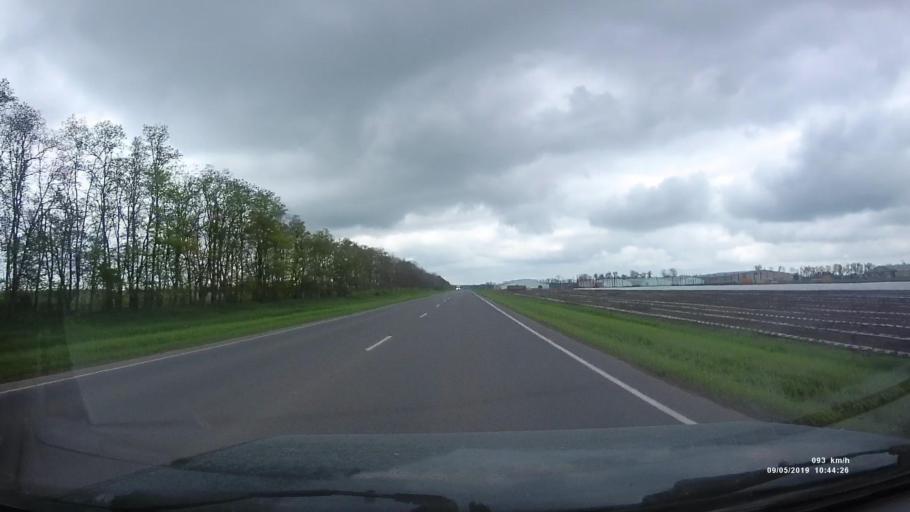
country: RU
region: Rostov
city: Peshkovo
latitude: 47.0014
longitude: 39.3880
